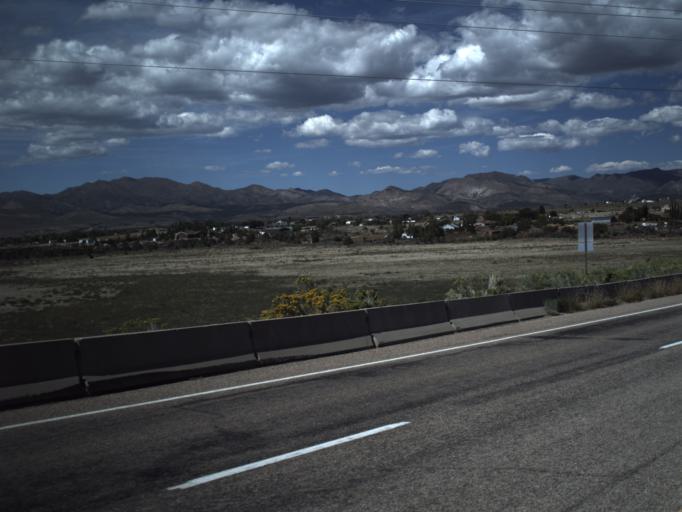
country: US
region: Utah
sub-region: Washington County
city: Ivins
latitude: 37.3266
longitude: -113.6932
